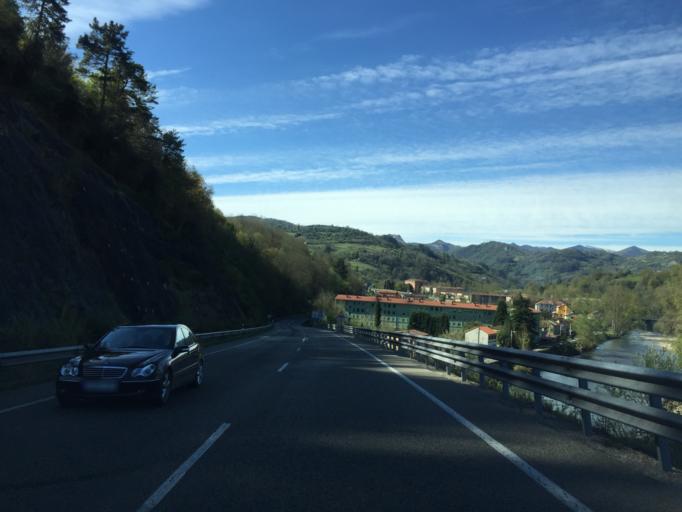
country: ES
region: Asturias
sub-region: Province of Asturias
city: Castandiello
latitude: 43.3570
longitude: -5.9599
